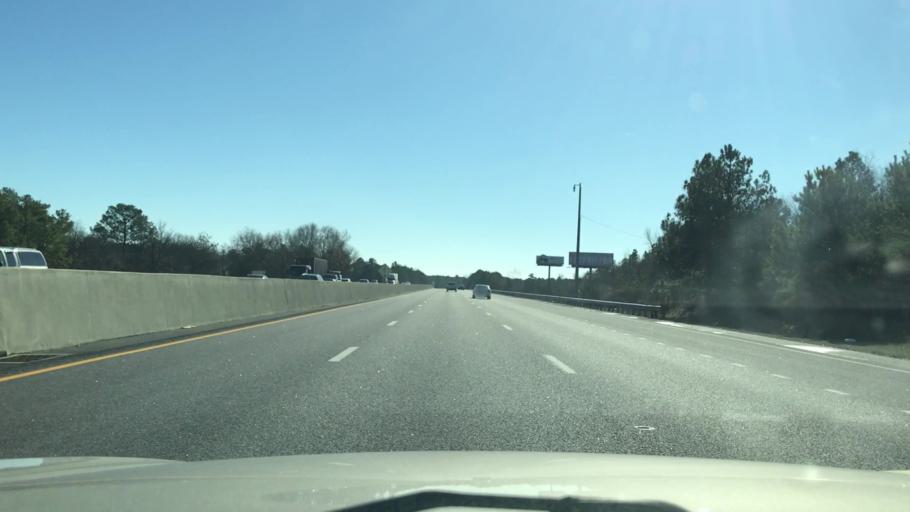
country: US
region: South Carolina
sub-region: Lexington County
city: Pineridge
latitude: 33.9185
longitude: -81.0645
